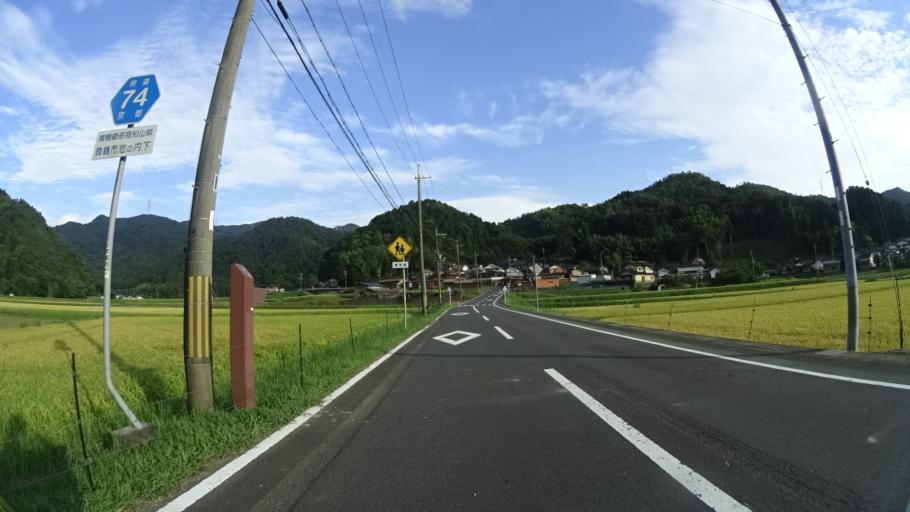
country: JP
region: Kyoto
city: Maizuru
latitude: 35.4099
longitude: 135.3462
